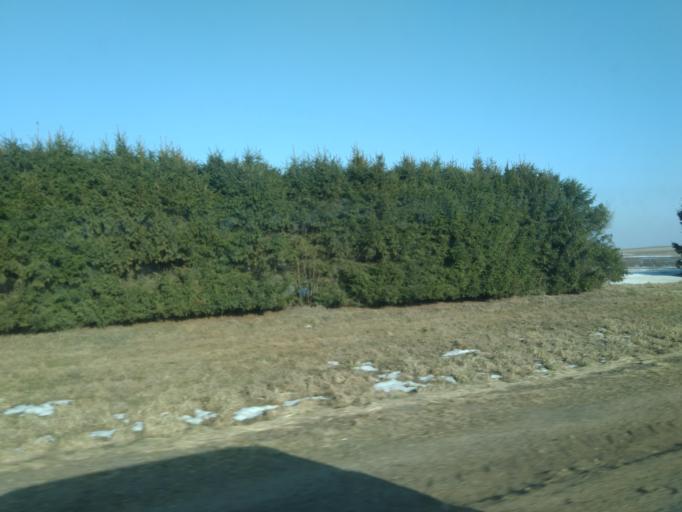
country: BY
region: Minsk
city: Snow
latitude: 53.2101
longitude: 26.4712
